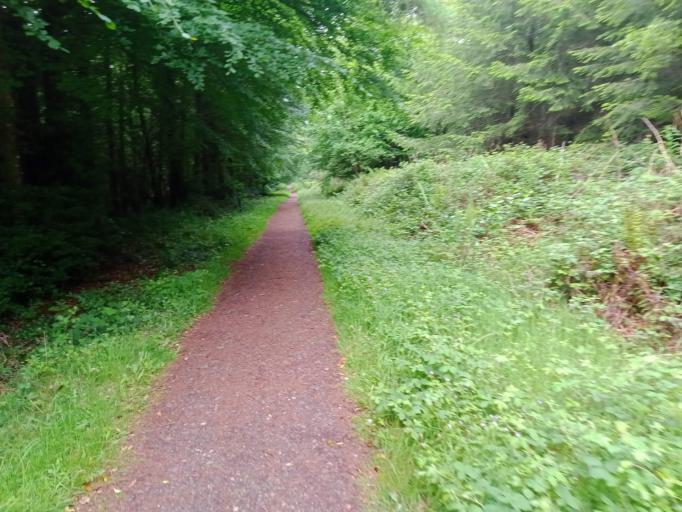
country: IE
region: Leinster
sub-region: Laois
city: Stradbally
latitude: 52.9963
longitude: -7.1215
